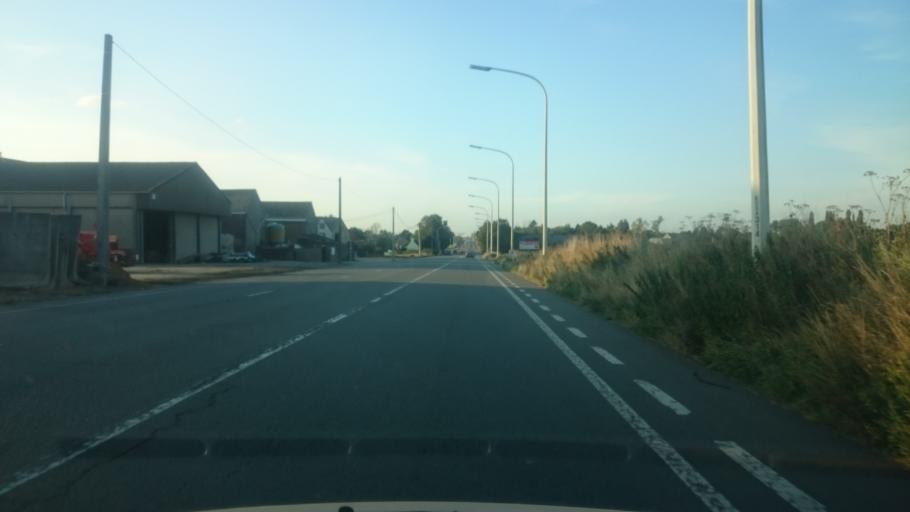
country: BE
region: Wallonia
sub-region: Province de Namur
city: Gembloux
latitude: 50.5879
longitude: 4.6817
